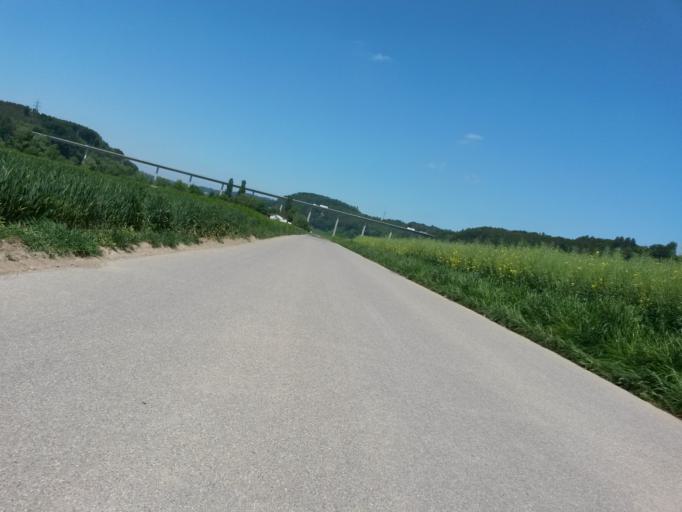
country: CH
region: Bern
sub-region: Bern-Mittelland District
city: Muhleberg
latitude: 46.9537
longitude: 7.2408
